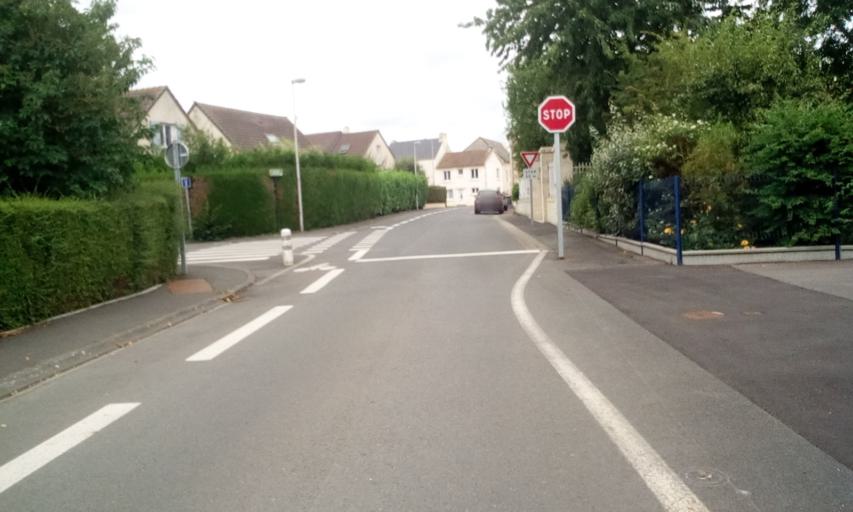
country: FR
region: Lower Normandy
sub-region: Departement du Calvados
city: Tourville-sur-Odon
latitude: 49.1397
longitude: -0.5045
